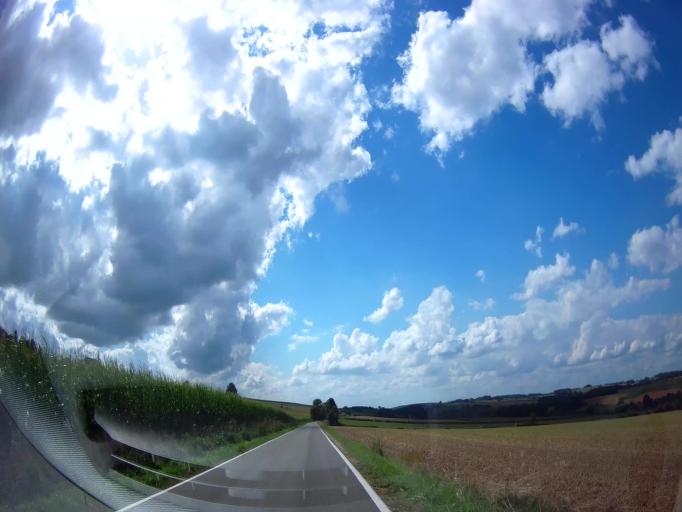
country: BE
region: Wallonia
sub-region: Province de Namur
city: Assesse
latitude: 50.3568
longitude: 4.9878
